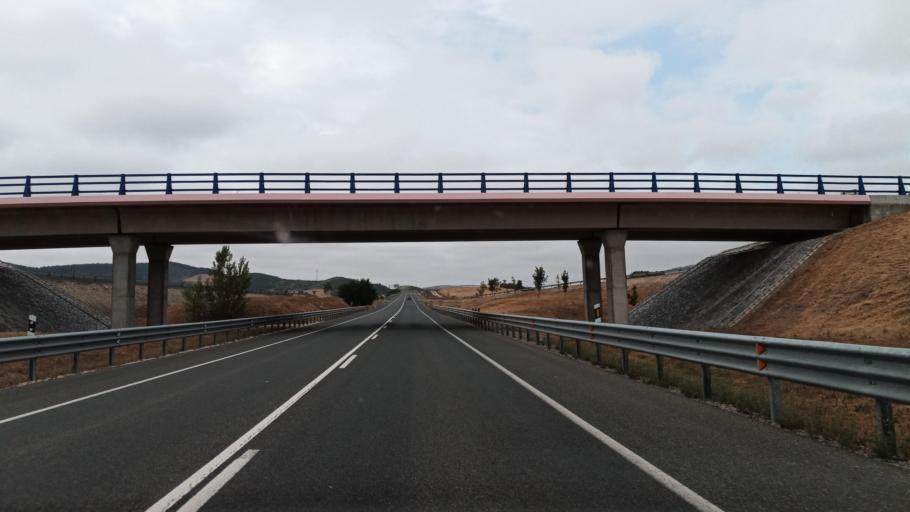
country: ES
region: Castille and Leon
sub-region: Provincia de Burgos
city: Quintanavides
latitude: 42.4773
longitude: -3.4180
